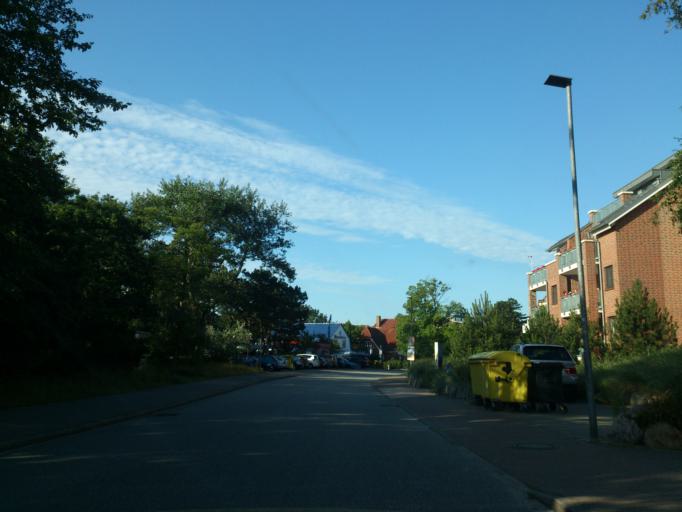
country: DE
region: Schleswig-Holstein
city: Sankt Peter-Ording
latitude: 54.3168
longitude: 8.6088
